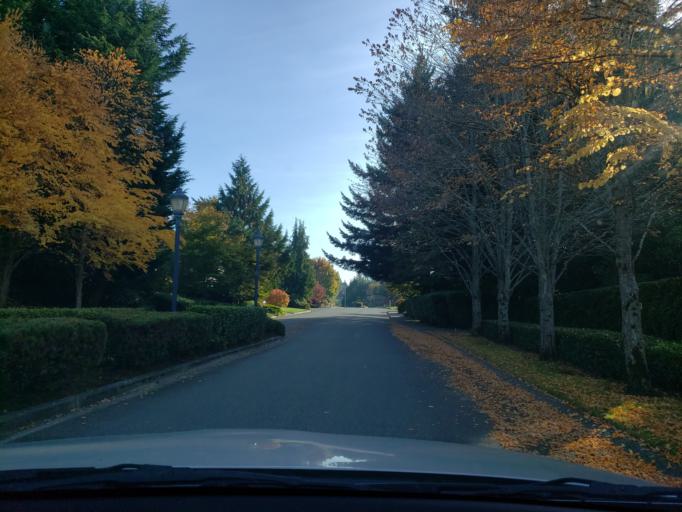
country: US
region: Washington
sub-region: Snohomish County
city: Meadowdale
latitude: 47.8757
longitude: -122.3210
